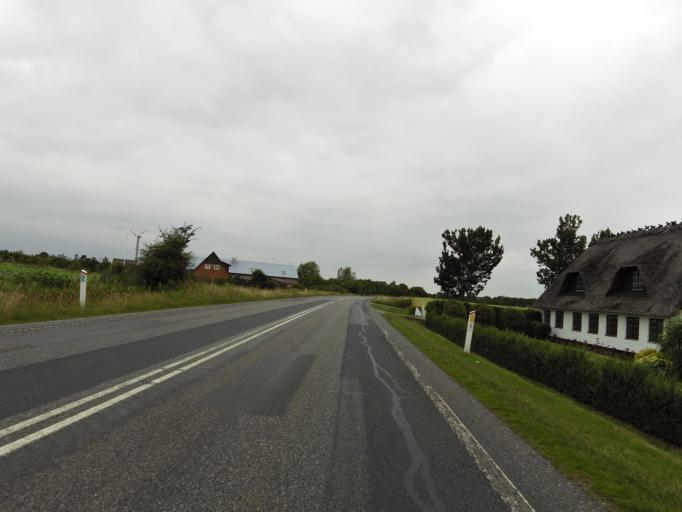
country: DK
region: South Denmark
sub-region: Tonder Kommune
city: Logumkloster
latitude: 55.1434
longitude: 8.9674
